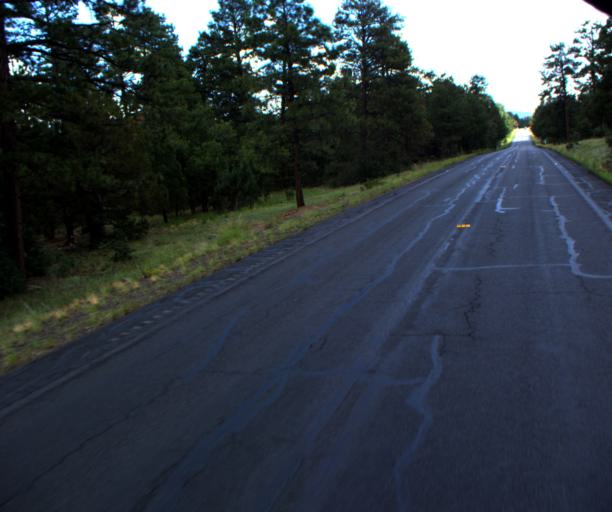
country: US
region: Arizona
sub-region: Gila County
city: Pine
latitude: 34.5050
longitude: -111.4700
